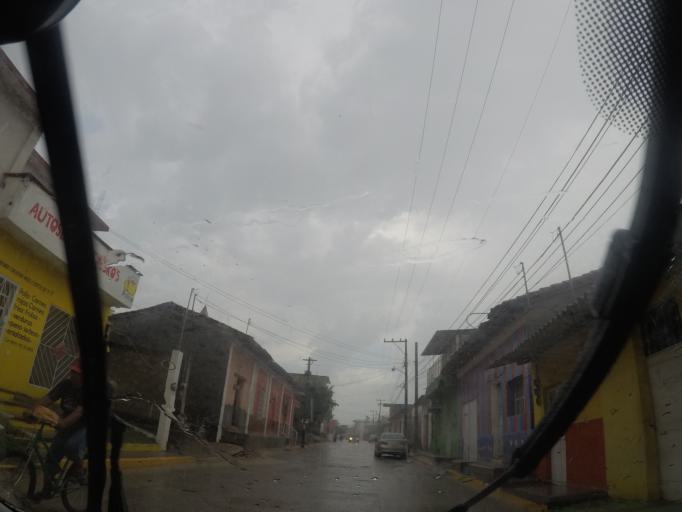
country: MX
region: Oaxaca
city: San Pedro Tapanatepec
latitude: 16.3674
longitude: -94.1954
